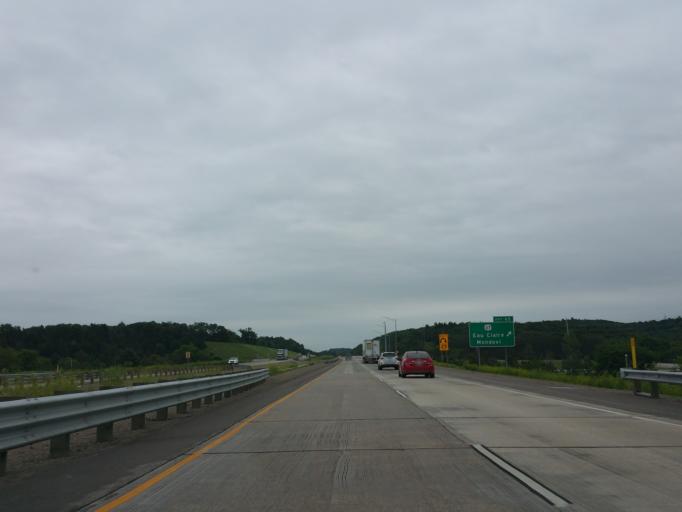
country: US
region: Wisconsin
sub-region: Eau Claire County
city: Eau Claire
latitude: 44.7800
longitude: -91.5362
